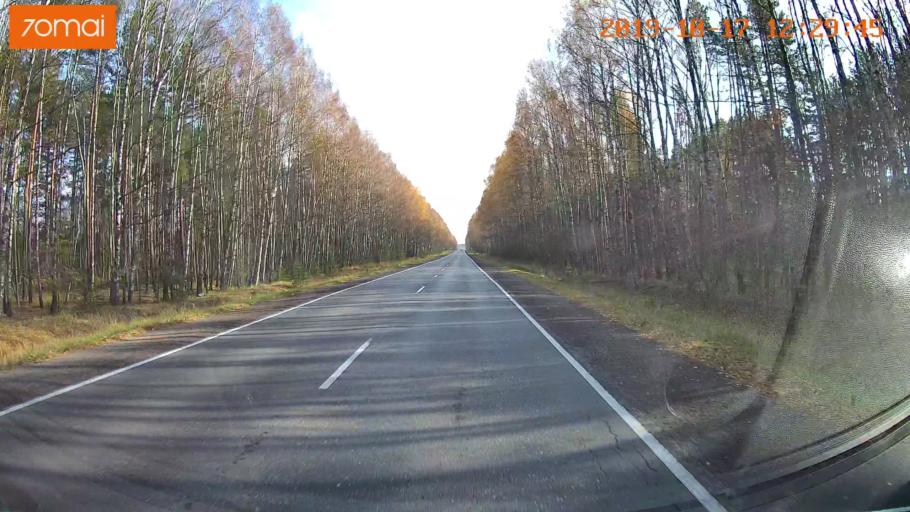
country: RU
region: Rjazan
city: Syntul
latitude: 54.9794
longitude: 41.2997
